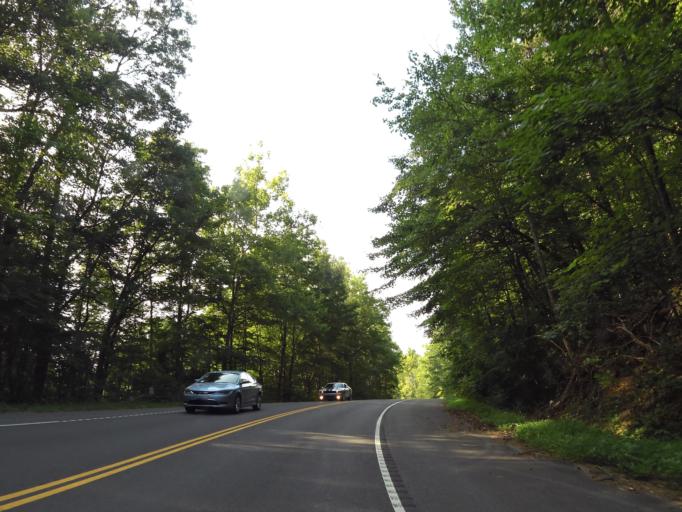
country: US
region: Tennessee
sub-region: Anderson County
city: Oak Ridge
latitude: 35.9123
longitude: -84.3323
